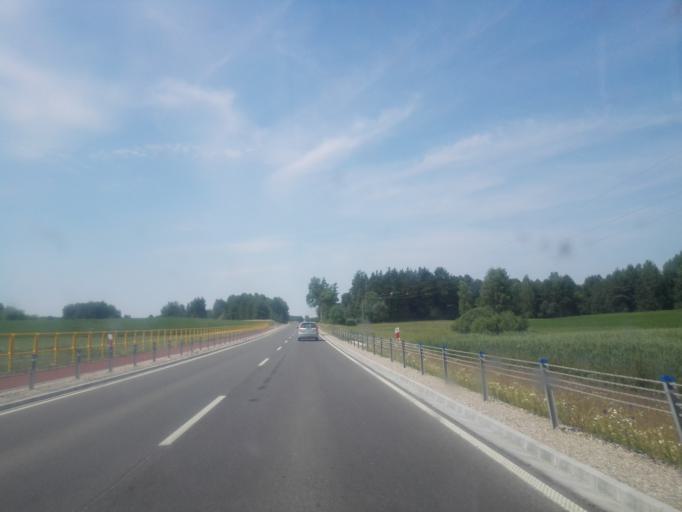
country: PL
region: Podlasie
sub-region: Powiat sejnenski
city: Krasnopol
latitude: 54.1085
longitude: 23.2732
